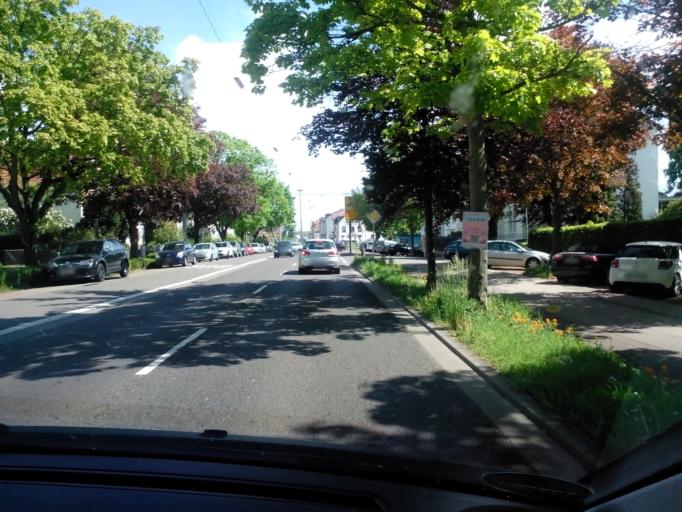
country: DE
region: Saarland
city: Saarlouis
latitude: 49.3092
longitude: 6.7463
